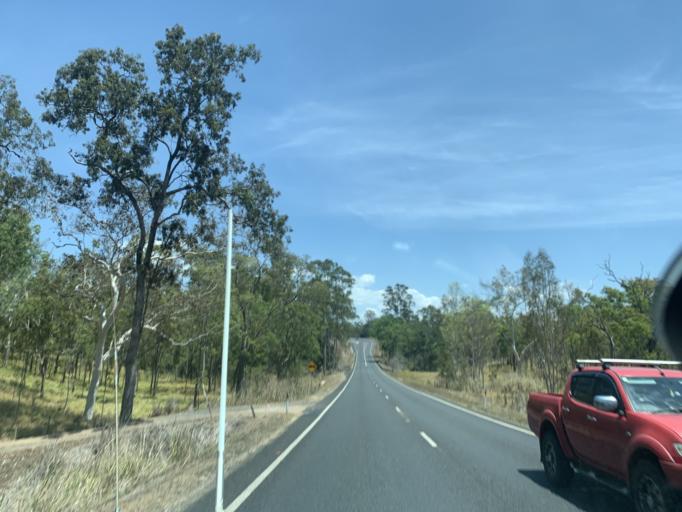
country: AU
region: Queensland
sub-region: Tablelands
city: Mareeba
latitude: -16.9641
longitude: 145.5372
